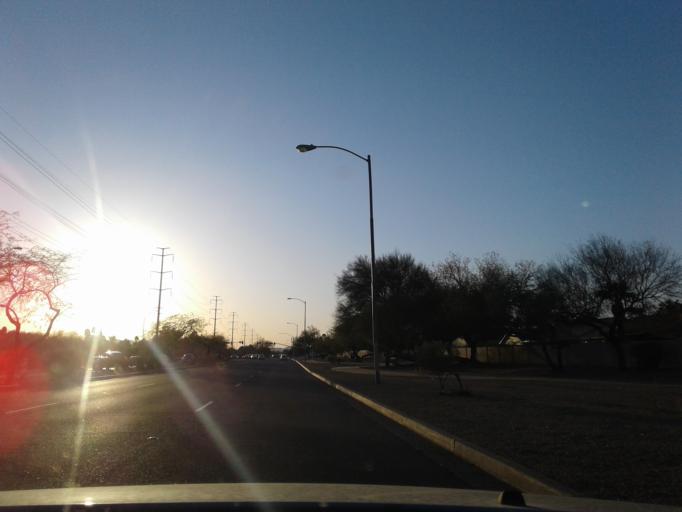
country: US
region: Arizona
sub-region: Maricopa County
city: Scottsdale
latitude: 33.5826
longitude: -111.8488
